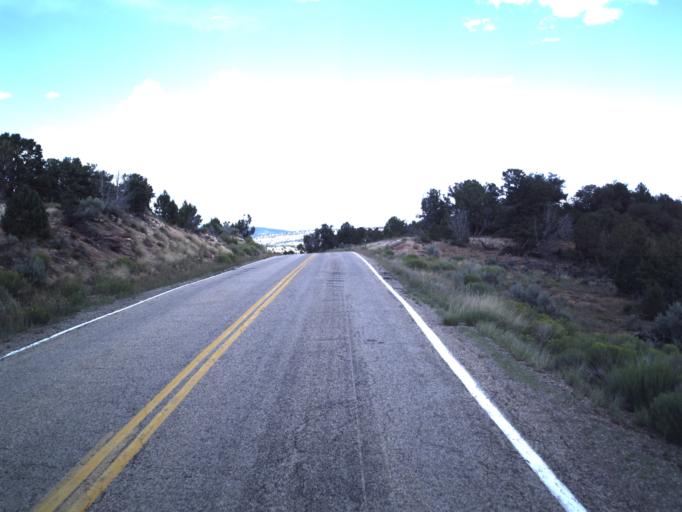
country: US
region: Utah
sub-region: Duchesne County
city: Duchesne
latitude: 40.2633
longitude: -110.7076
